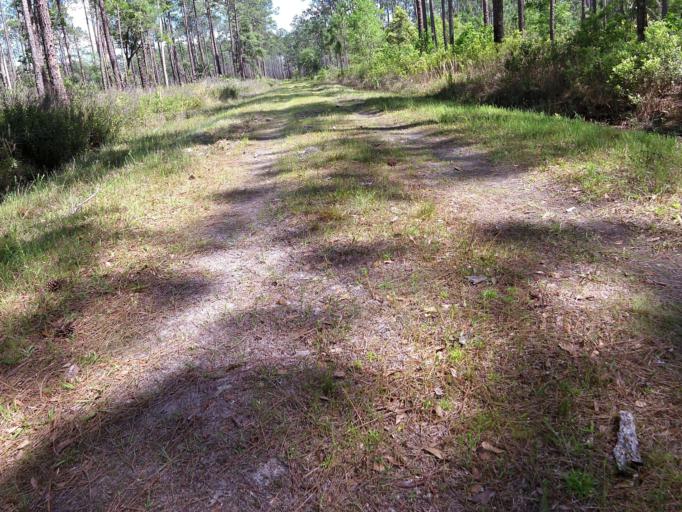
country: US
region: Florida
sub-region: Clay County
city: Green Cove Springs
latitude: 29.9635
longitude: -81.6336
